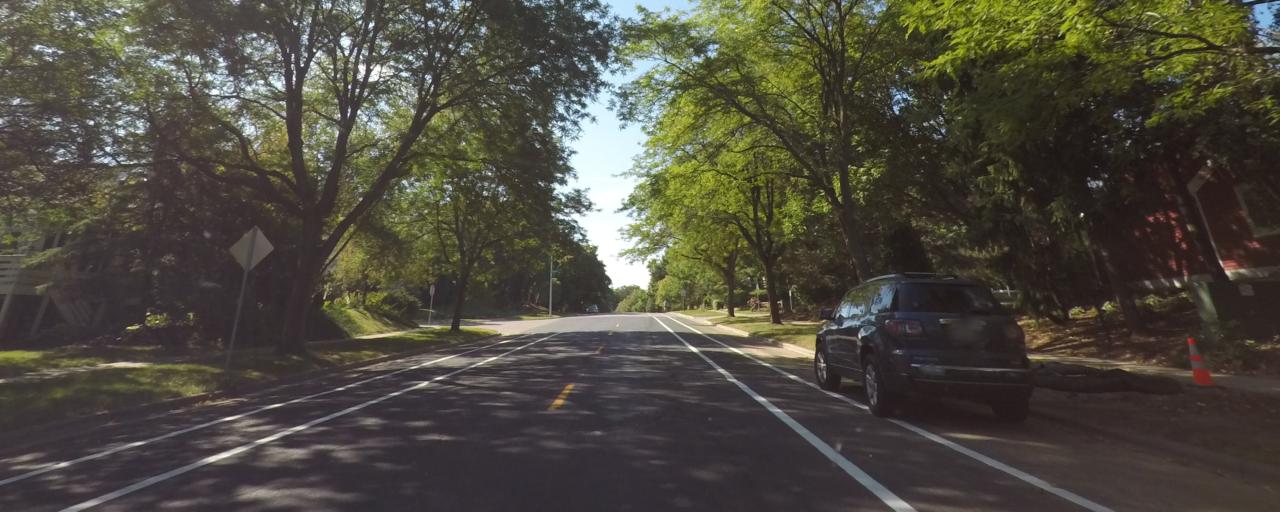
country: US
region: Wisconsin
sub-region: Dane County
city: Middleton
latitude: 43.0681
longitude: -89.5086
